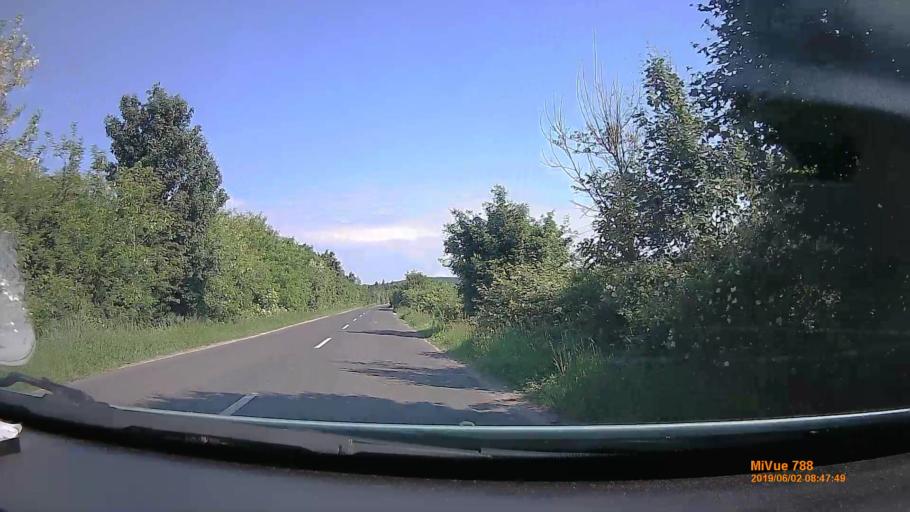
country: HU
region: Borsod-Abauj-Zemplen
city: Sajobabony
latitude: 48.1307
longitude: 20.7097
